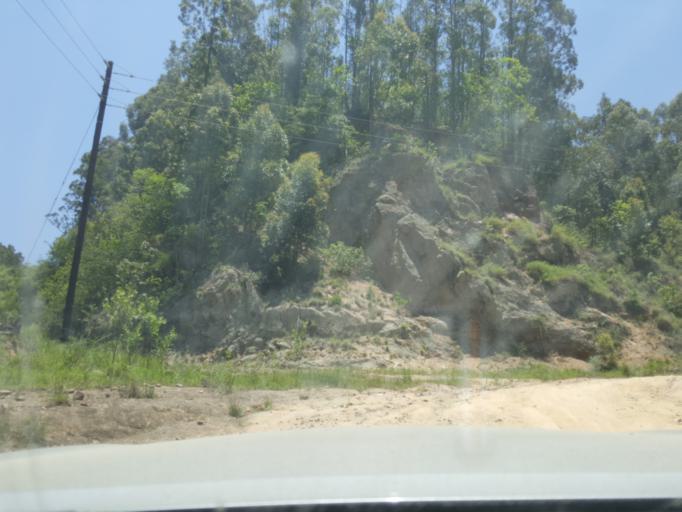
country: ZA
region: Limpopo
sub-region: Mopani District Municipality
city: Hoedspruit
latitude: -24.5963
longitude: 30.8741
